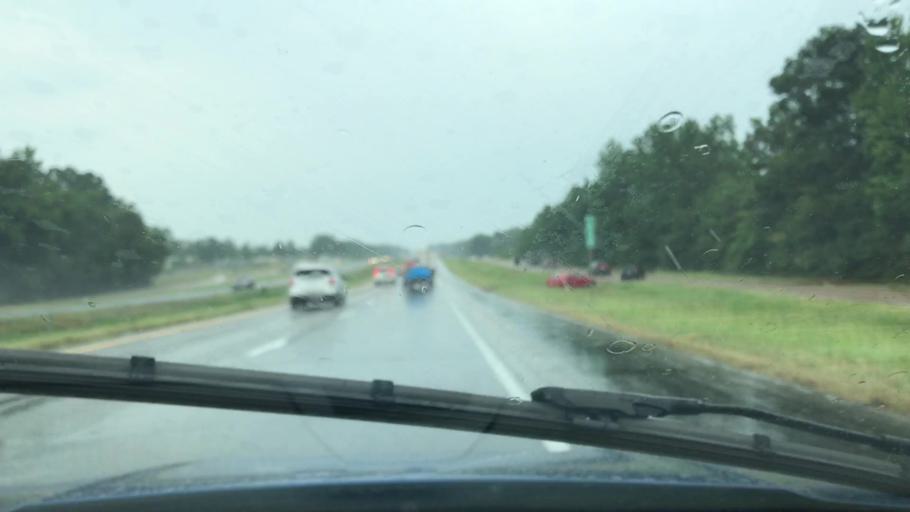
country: US
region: Texas
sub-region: Harrison County
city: Waskom
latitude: 32.4893
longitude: -94.1418
